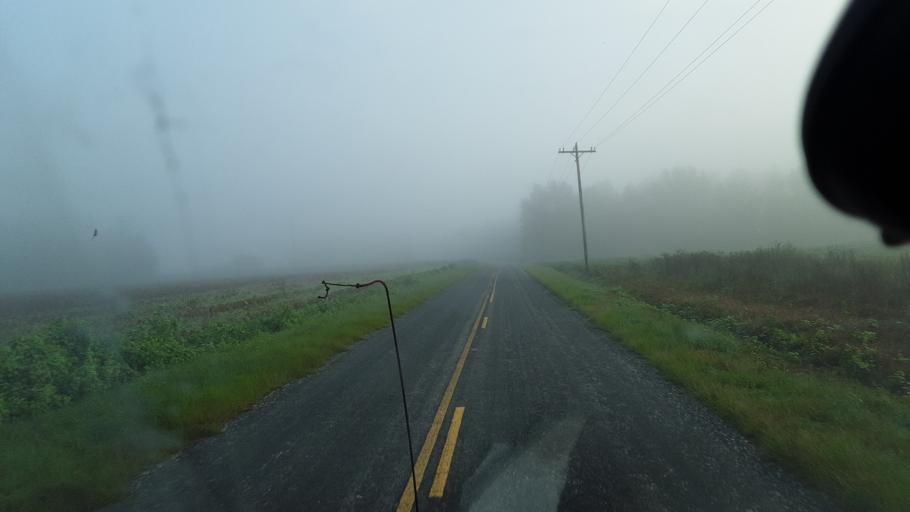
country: US
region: South Carolina
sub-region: Williamsburg County
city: Kingstree
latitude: 33.8103
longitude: -79.9631
